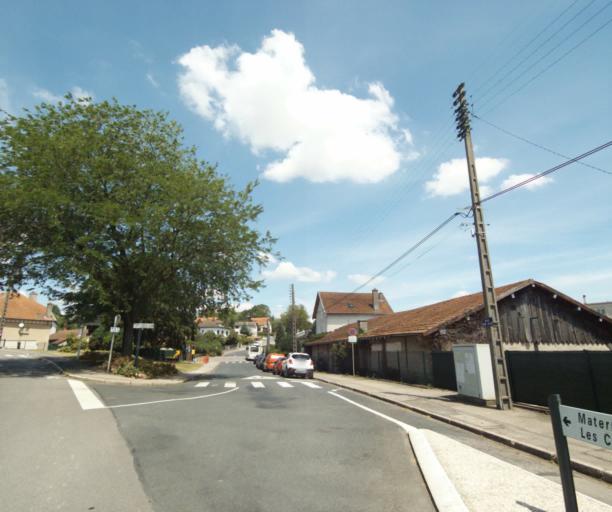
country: FR
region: Lorraine
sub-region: Departement de Meurthe-et-Moselle
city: Luneville
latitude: 48.6019
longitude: 6.4900
